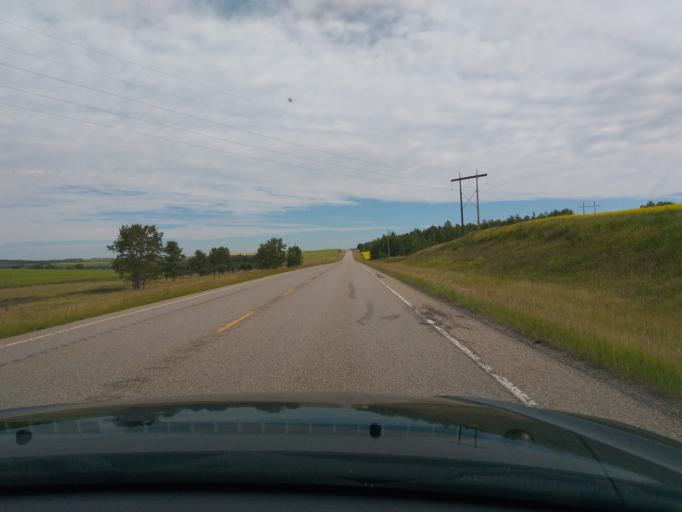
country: CA
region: Alberta
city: Cochrane
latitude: 51.4312
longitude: -114.4705
